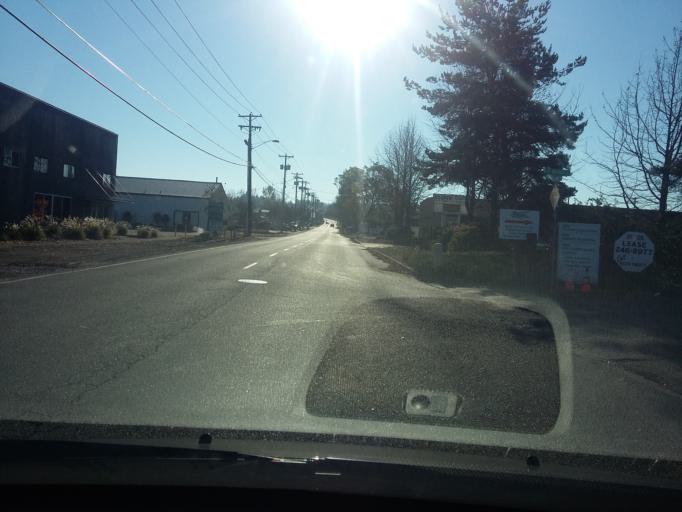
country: US
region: Oregon
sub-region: Multnomah County
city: Fairview
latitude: 45.5567
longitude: -122.5103
